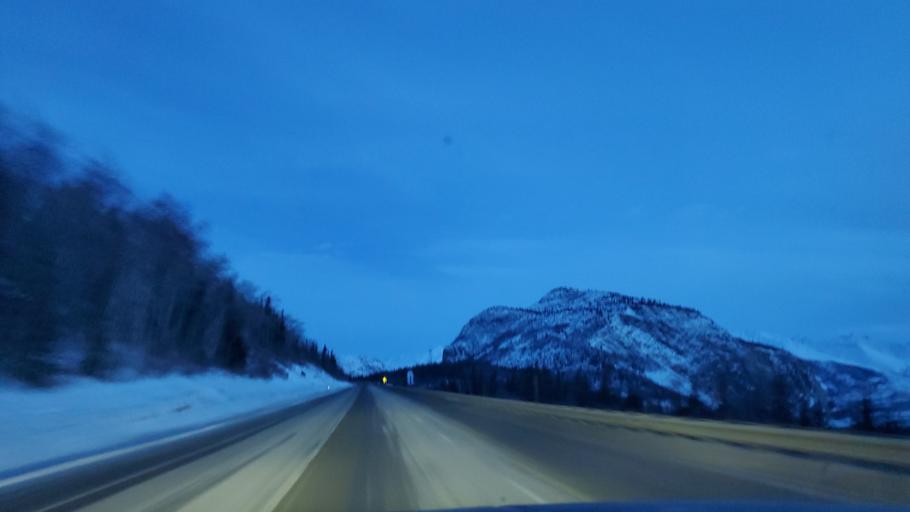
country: US
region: Alaska
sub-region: Matanuska-Susitna Borough
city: Sutton-Alpine
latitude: 61.7920
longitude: -147.7078
